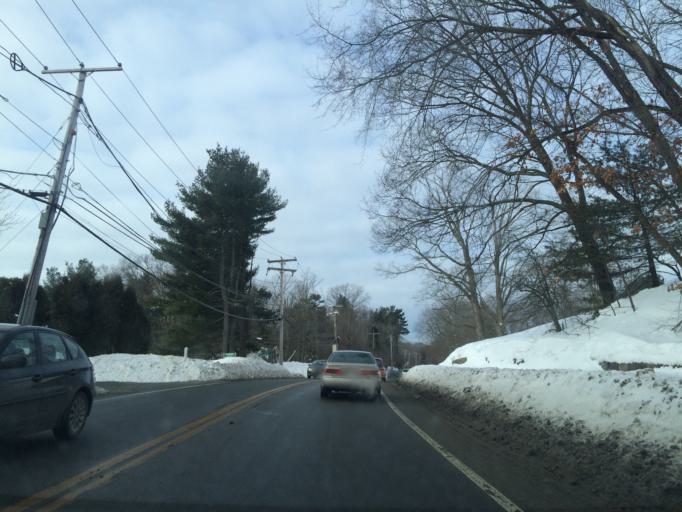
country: US
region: Massachusetts
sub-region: Middlesex County
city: Weston
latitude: 42.3676
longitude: -71.2750
